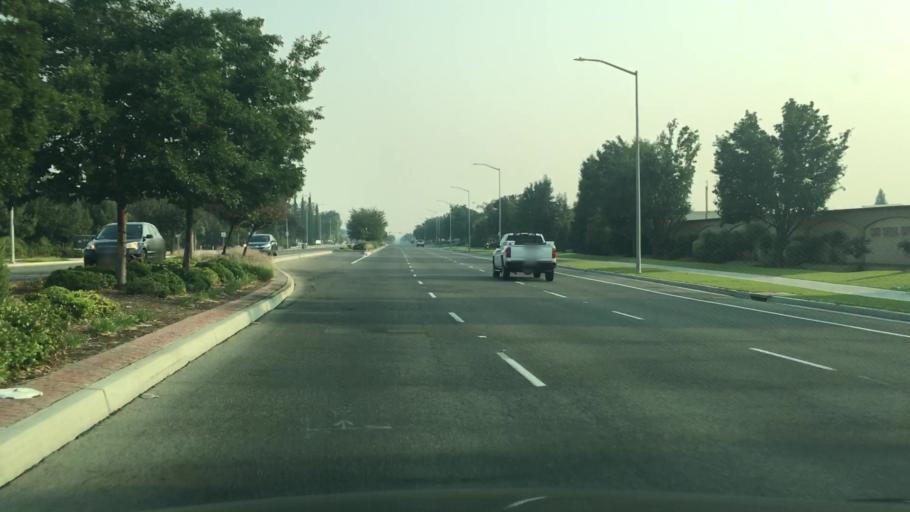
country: US
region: California
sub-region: Fresno County
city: Clovis
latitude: 36.8469
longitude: -119.7297
